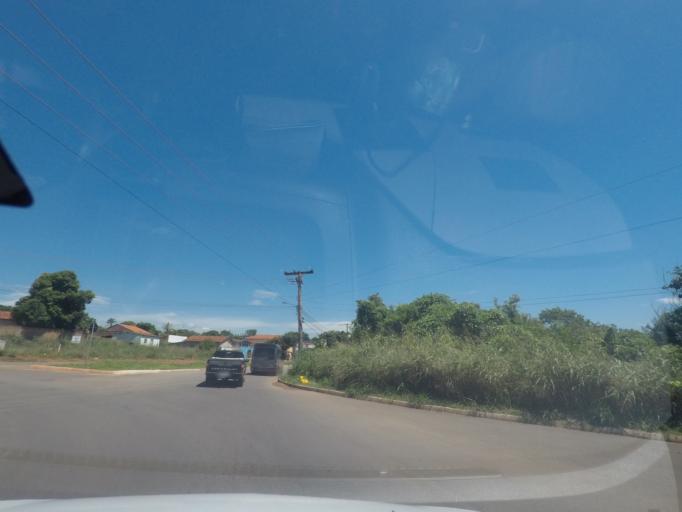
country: BR
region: Goias
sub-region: Aparecida De Goiania
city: Aparecida de Goiania
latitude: -16.7776
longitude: -49.3281
